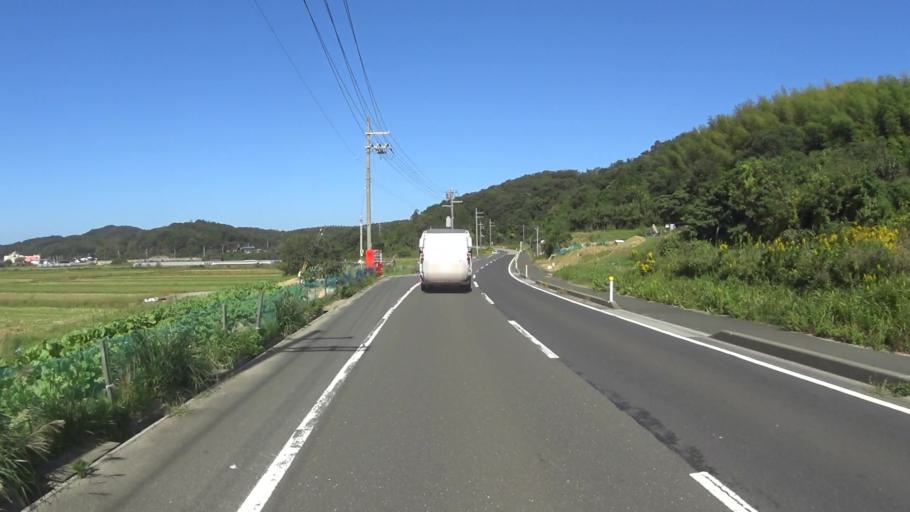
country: JP
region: Kyoto
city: Miyazu
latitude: 35.6900
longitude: 135.0517
